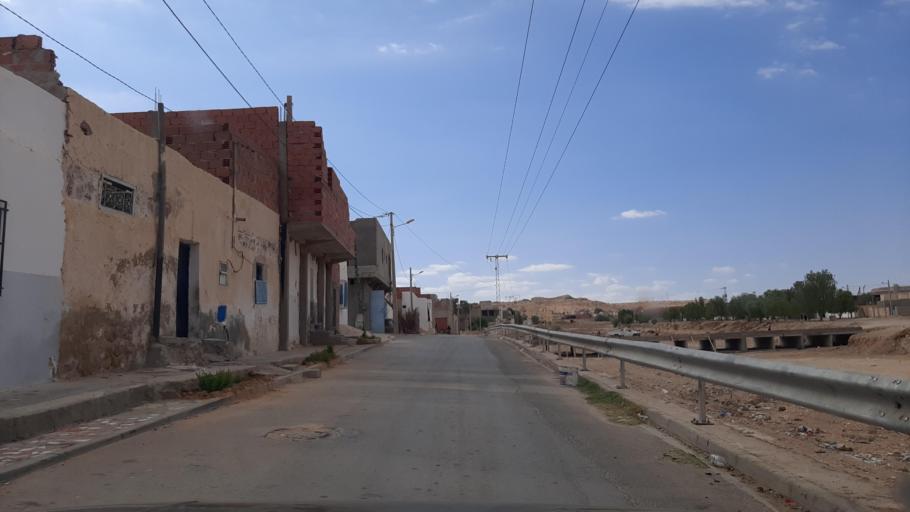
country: TN
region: Tataouine
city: Tataouine
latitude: 32.9390
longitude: 10.4510
